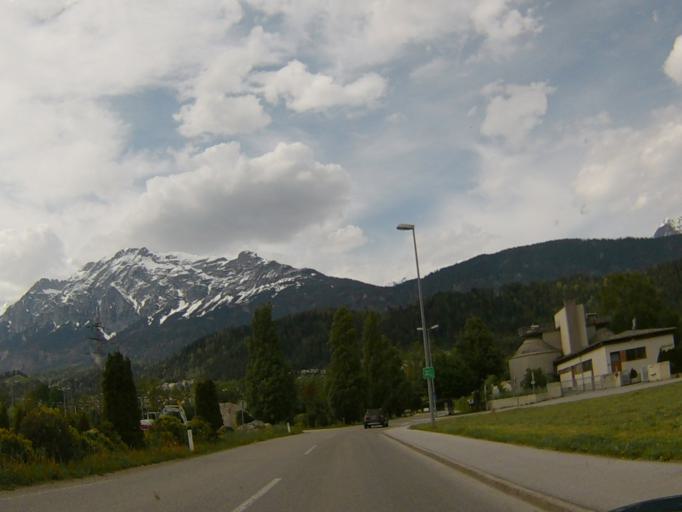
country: AT
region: Tyrol
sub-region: Politischer Bezirk Innsbruck Land
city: Wattenberg
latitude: 47.2968
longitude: 11.6046
